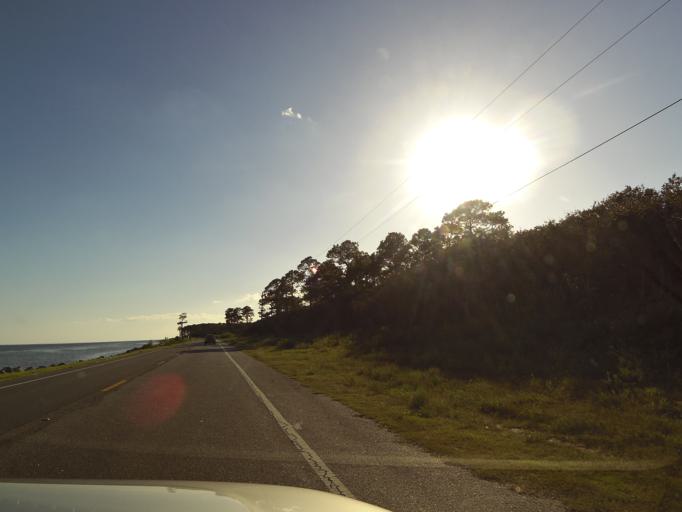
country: US
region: Florida
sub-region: Franklin County
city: Eastpoint
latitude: 29.7748
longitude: -84.7901
